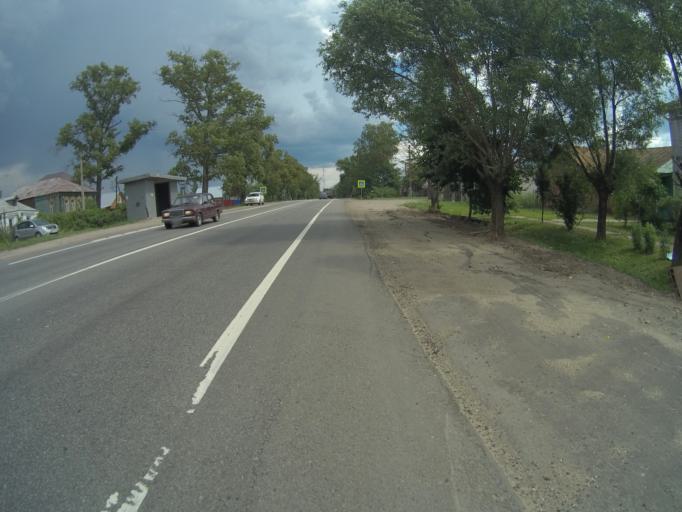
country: RU
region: Vladimir
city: Orgtrud
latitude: 56.2095
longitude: 40.6677
